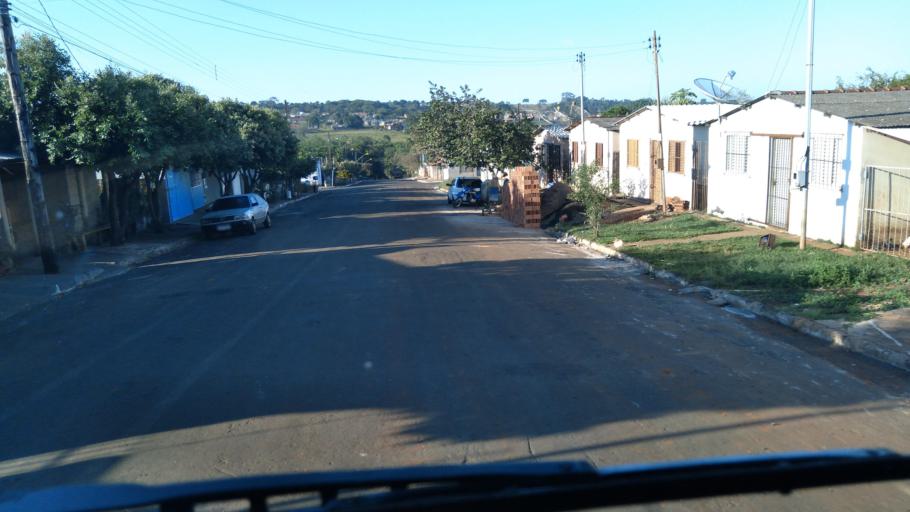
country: BR
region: Goias
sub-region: Mineiros
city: Mineiros
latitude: -17.5741
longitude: -52.5632
